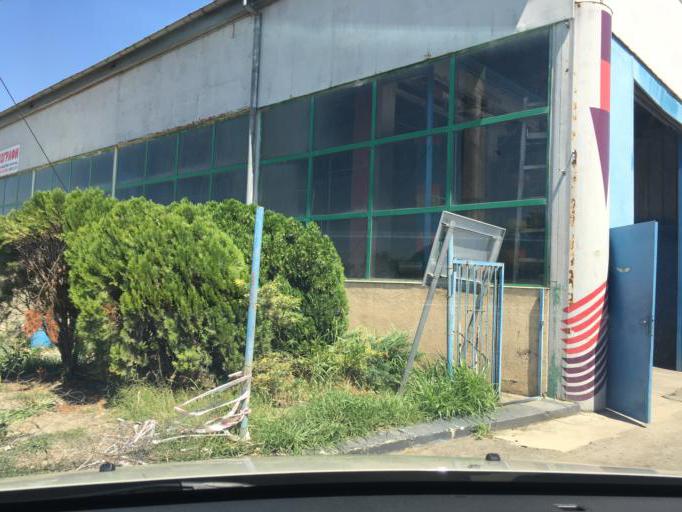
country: BG
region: Burgas
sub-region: Obshtina Burgas
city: Burgas
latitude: 42.5002
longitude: 27.4547
